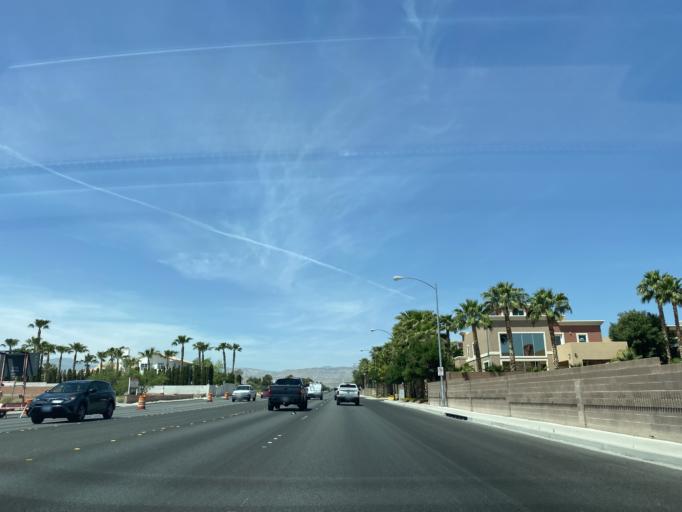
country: US
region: Nevada
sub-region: Clark County
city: Spring Valley
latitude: 36.0854
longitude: -115.2280
